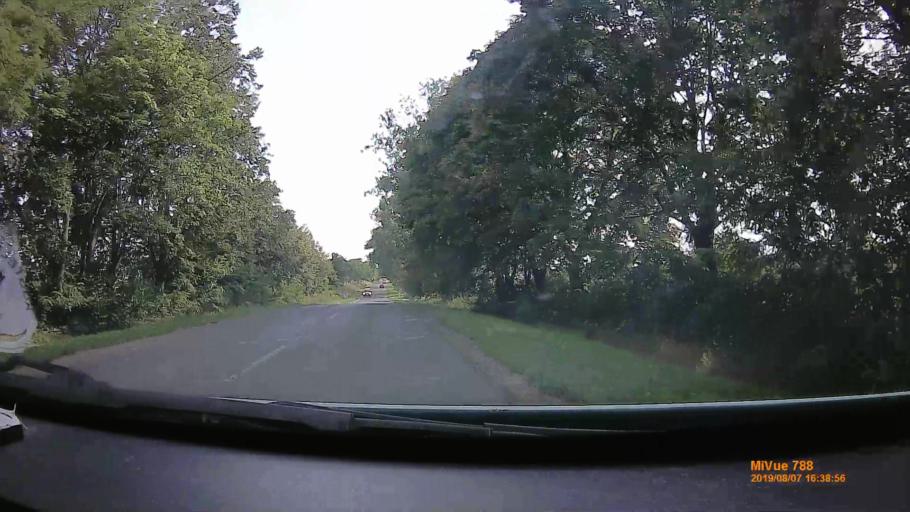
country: HU
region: Borsod-Abauj-Zemplen
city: Gonc
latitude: 48.3977
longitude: 21.2252
